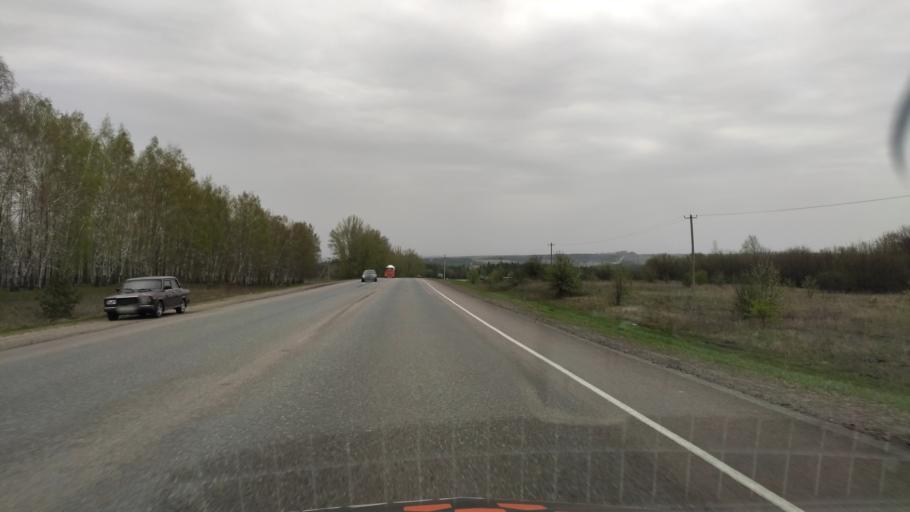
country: RU
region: Kursk
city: Gorshechnoye
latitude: 51.4597
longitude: 37.9232
